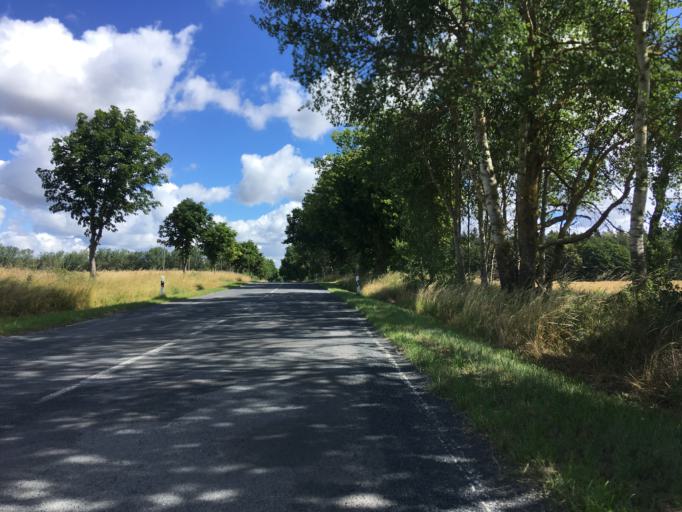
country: DE
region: Brandenburg
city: Mittenwalde
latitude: 53.1874
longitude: 13.5892
